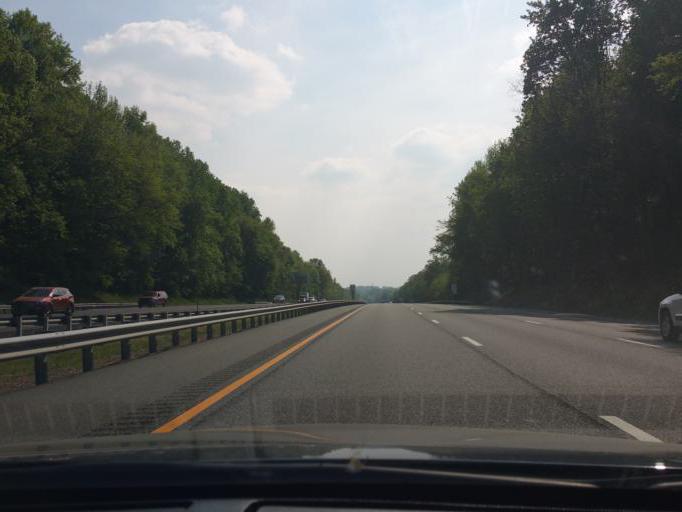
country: US
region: Maryland
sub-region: Harford County
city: Aberdeen
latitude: 39.5620
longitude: -76.1468
